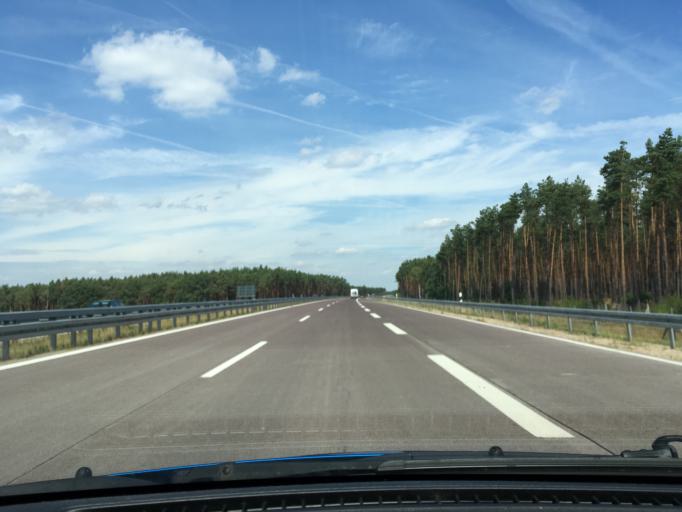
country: DE
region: Mecklenburg-Vorpommern
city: Ludwigslust
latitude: 53.3472
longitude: 11.5180
